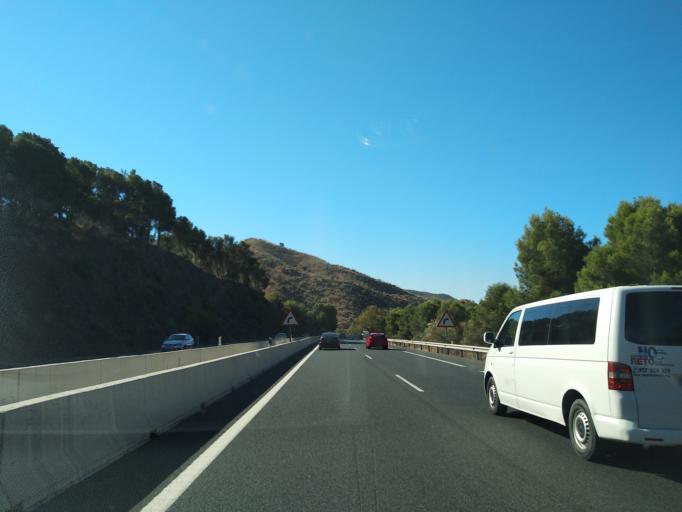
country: ES
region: Andalusia
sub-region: Provincia de Malaga
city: Malaga
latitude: 36.8028
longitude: -4.4356
